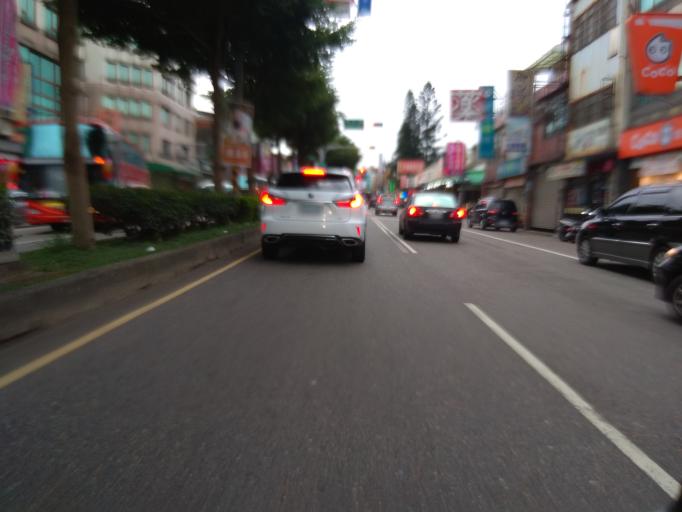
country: TW
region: Taiwan
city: Daxi
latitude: 24.9154
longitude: 121.2106
